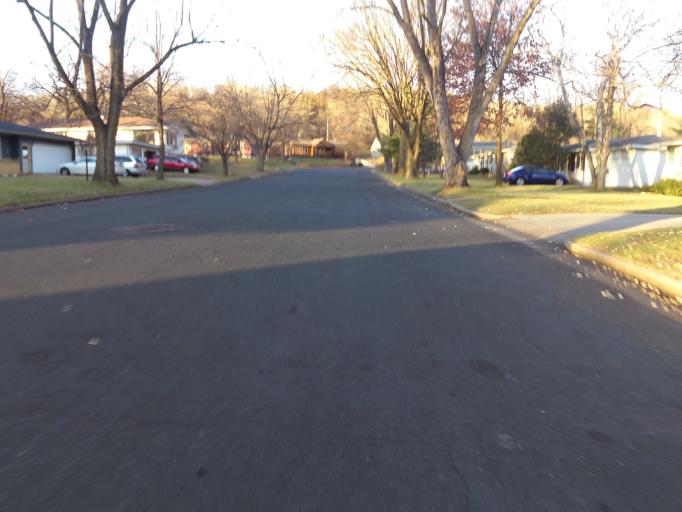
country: US
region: Wisconsin
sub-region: Pierce County
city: River Falls
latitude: 44.8634
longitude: -92.6178
